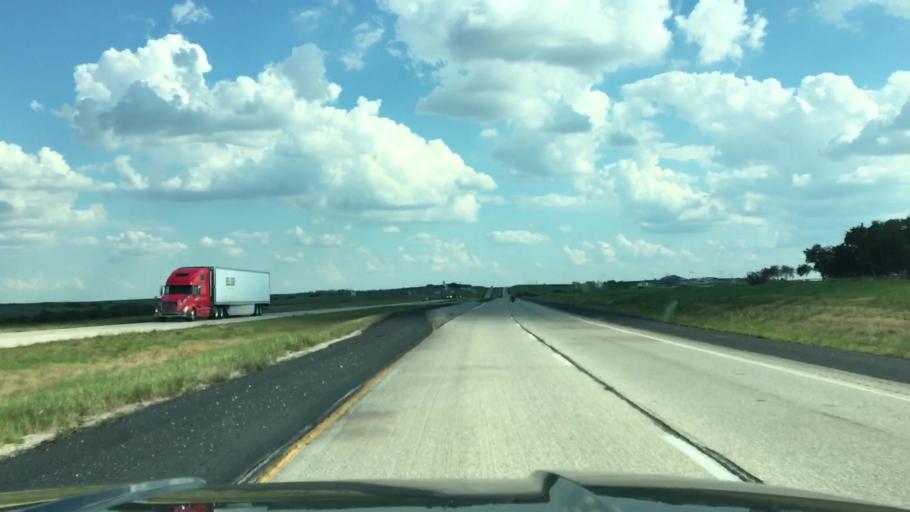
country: US
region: Texas
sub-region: Wise County
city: New Fairview
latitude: 33.1425
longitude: -97.4990
